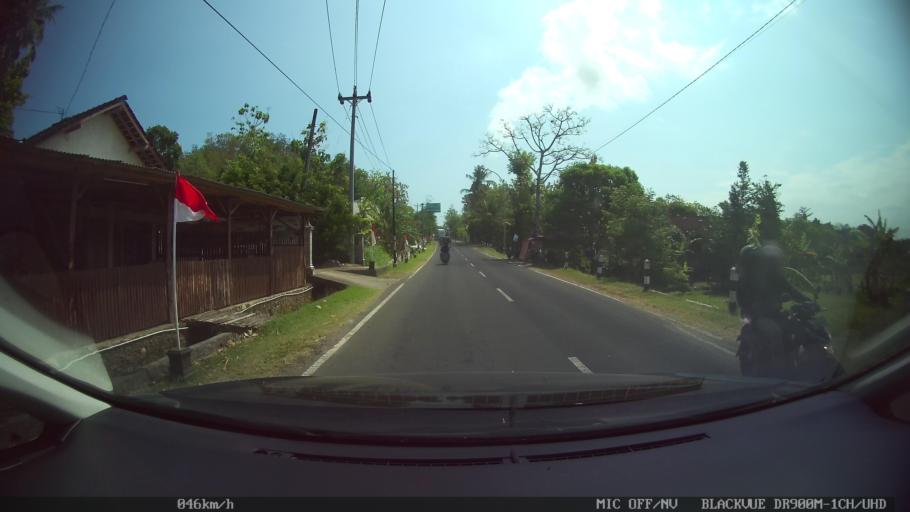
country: ID
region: Daerah Istimewa Yogyakarta
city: Pundong
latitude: -7.9870
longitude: 110.3262
